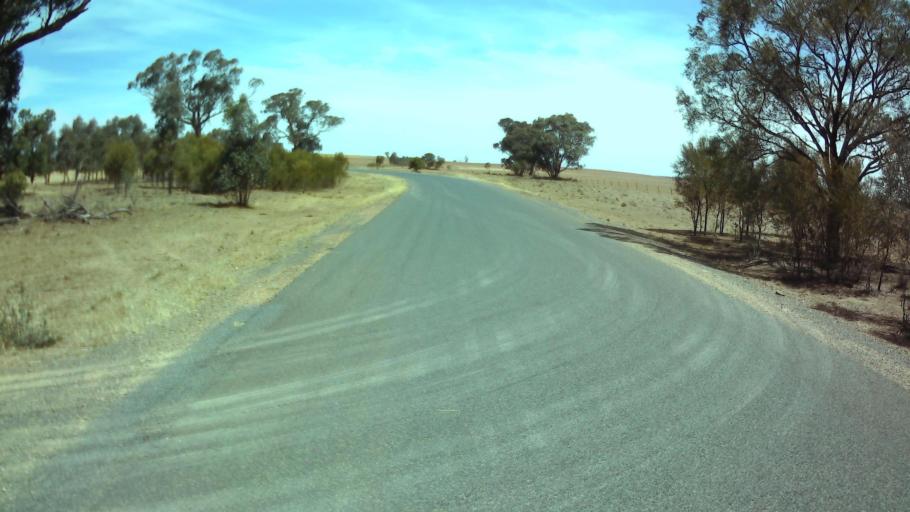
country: AU
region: New South Wales
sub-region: Weddin
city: Grenfell
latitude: -33.8865
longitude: 147.7419
